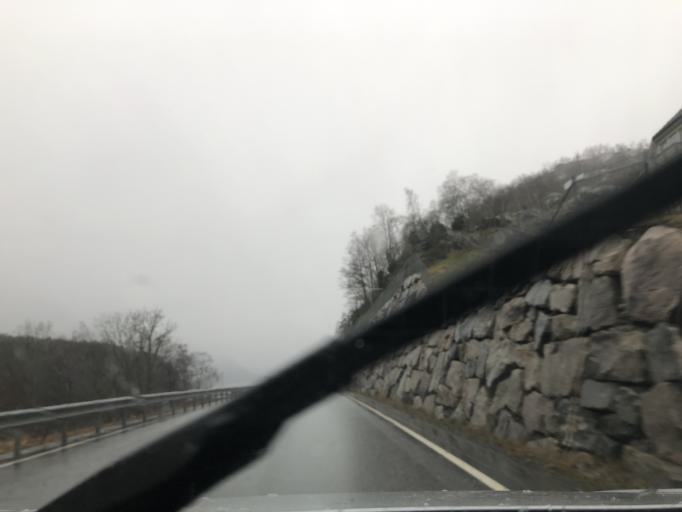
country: NO
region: Rogaland
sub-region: Hjelmeland
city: Hjelmelandsvagen
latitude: 59.3207
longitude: 6.2824
